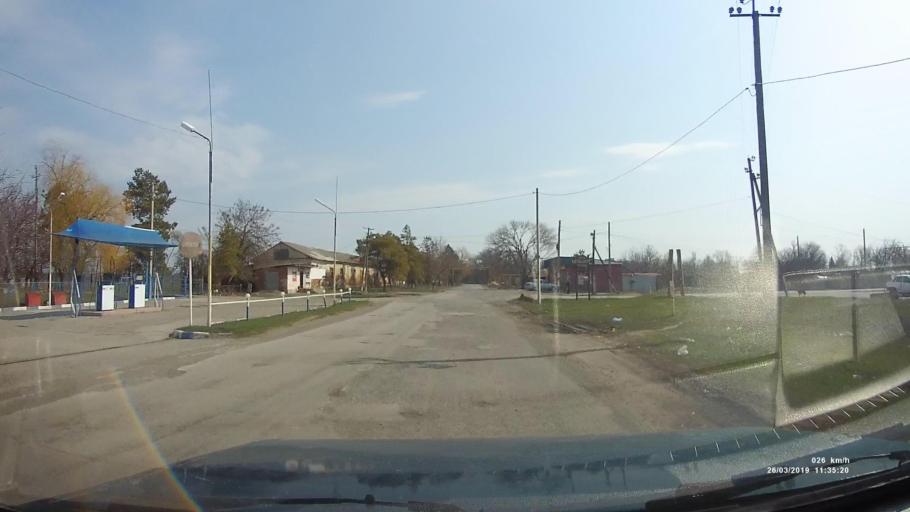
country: RU
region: Rostov
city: Novobessergenovka
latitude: 47.1468
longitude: 38.6364
